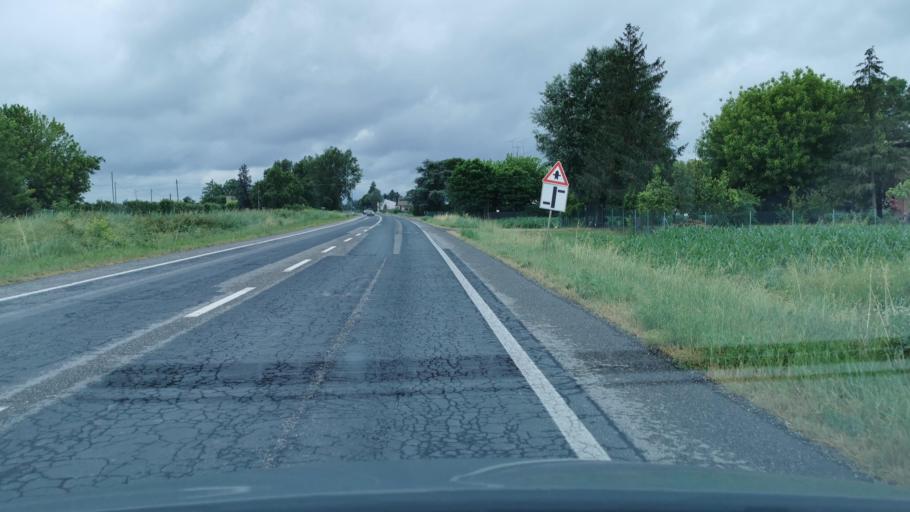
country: IT
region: Emilia-Romagna
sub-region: Provincia di Ravenna
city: Bagnacavallo
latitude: 44.3984
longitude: 11.9606
